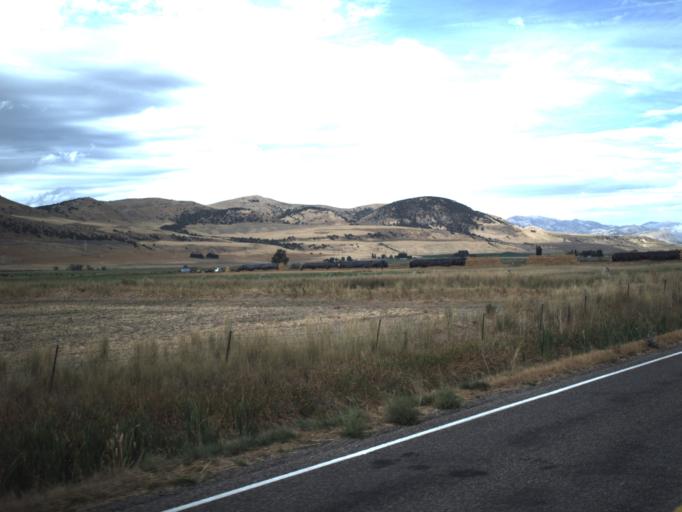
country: US
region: Utah
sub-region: Cache County
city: Lewiston
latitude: 41.9554
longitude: -111.9539
